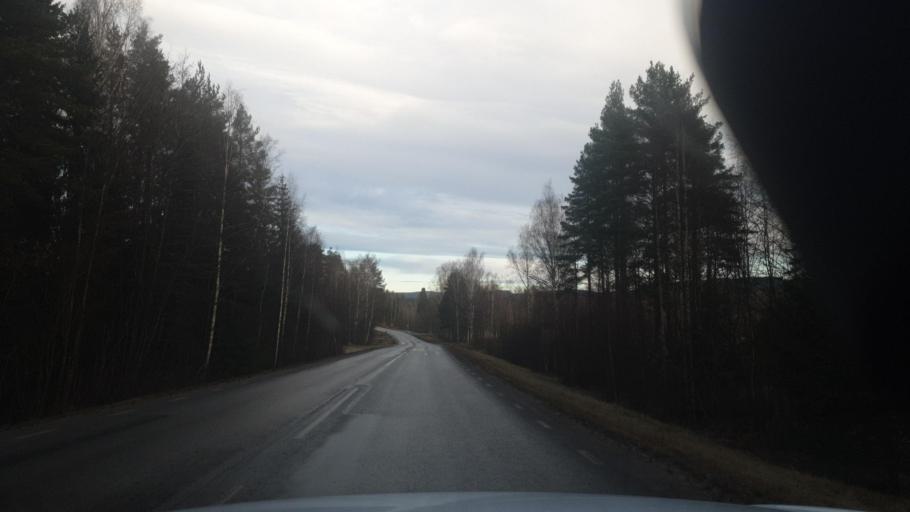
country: SE
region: Vaermland
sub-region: Arvika Kommun
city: Arvika
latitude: 59.6708
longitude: 12.6265
